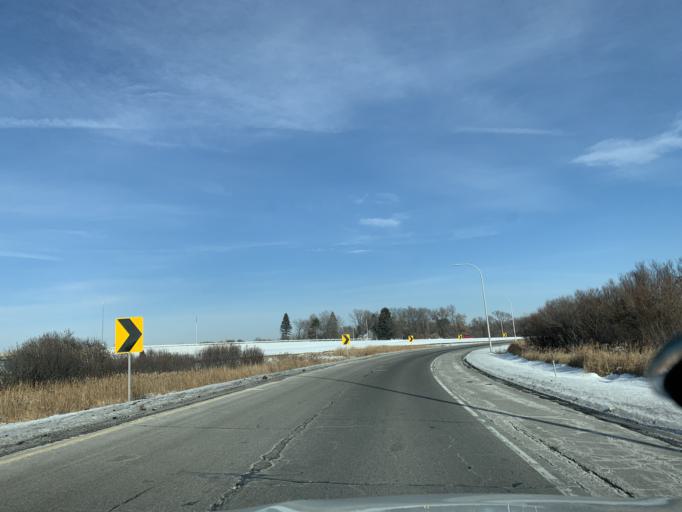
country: US
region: Minnesota
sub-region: Washington County
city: Forest Lake
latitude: 45.2880
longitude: -93.0024
